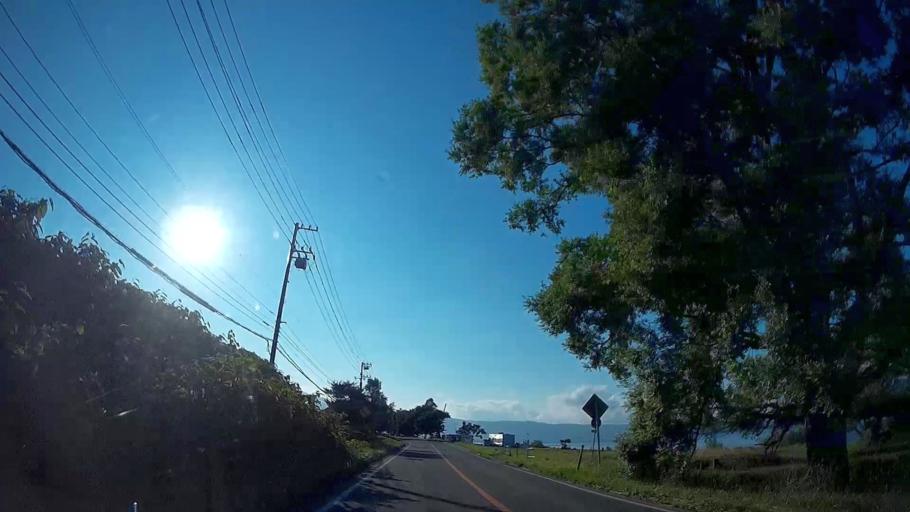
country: JP
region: Hokkaido
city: Date
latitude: 42.5630
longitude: 140.8456
